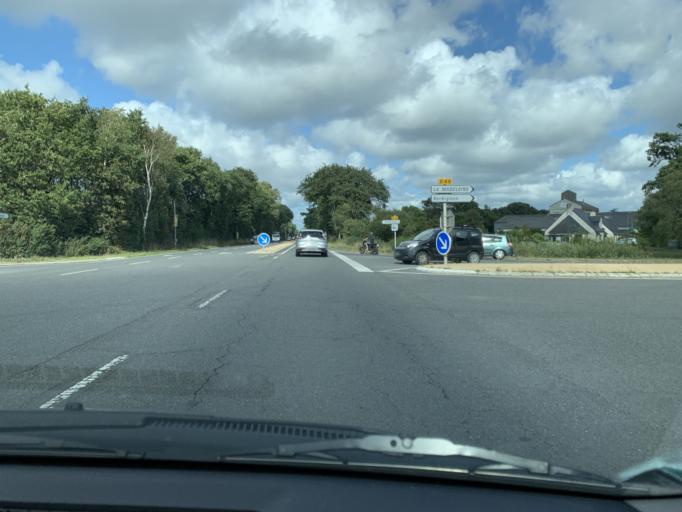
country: FR
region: Pays de la Loire
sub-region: Departement de la Loire-Atlantique
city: Saint-Molf
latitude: 47.3739
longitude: -2.4008
